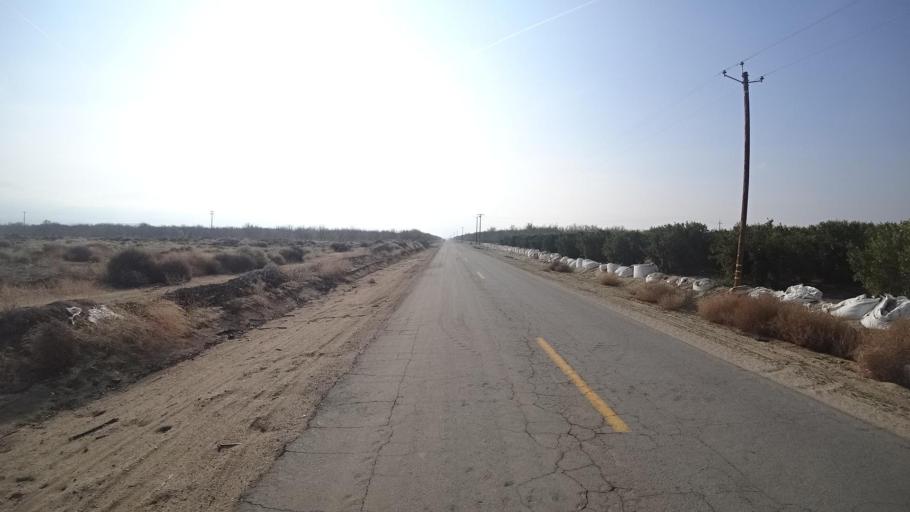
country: US
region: California
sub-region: Kern County
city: Lebec
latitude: 35.0100
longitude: -118.8466
